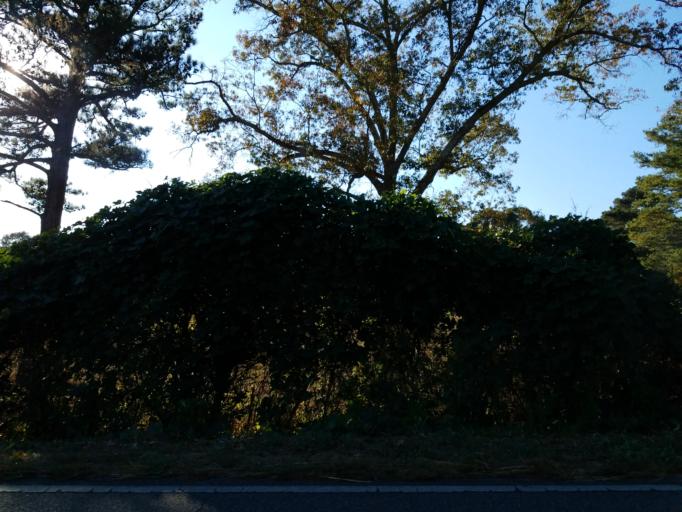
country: US
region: Georgia
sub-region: Pickens County
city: Jasper
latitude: 34.5784
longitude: -84.4575
